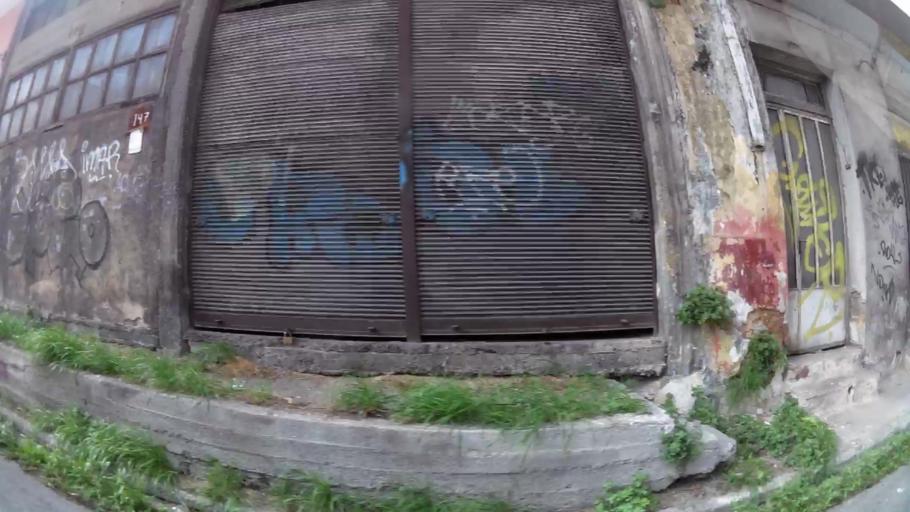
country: GR
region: Attica
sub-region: Nomos Piraios
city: Nikaia
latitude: 37.9634
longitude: 23.6385
